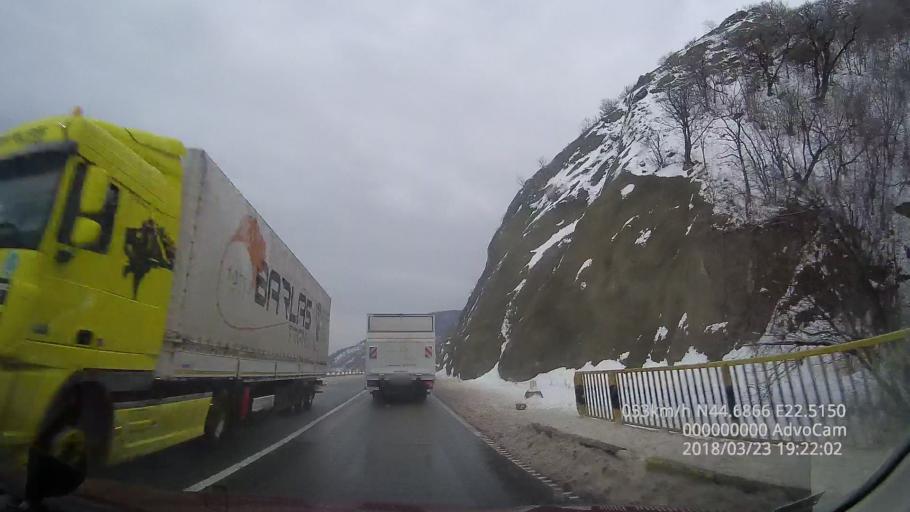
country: RO
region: Mehedinti
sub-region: Municipiul Drobeta-Turnu Severin
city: Gura Vaii
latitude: 44.6868
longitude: 22.5149
